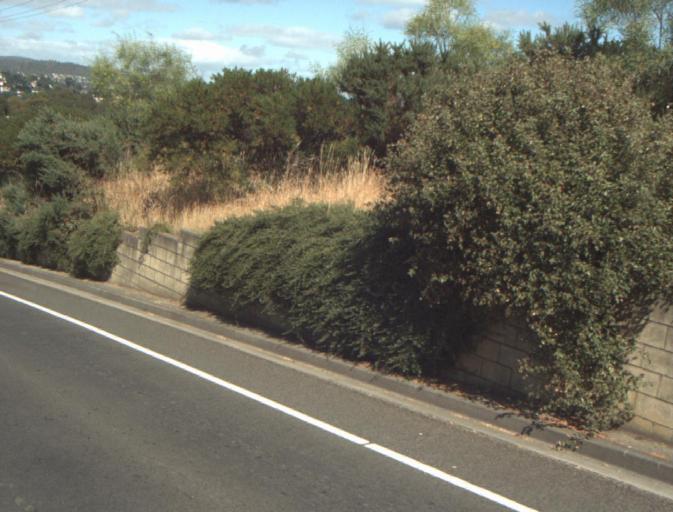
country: AU
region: Tasmania
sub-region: Launceston
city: Newstead
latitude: -41.4299
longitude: 147.1748
